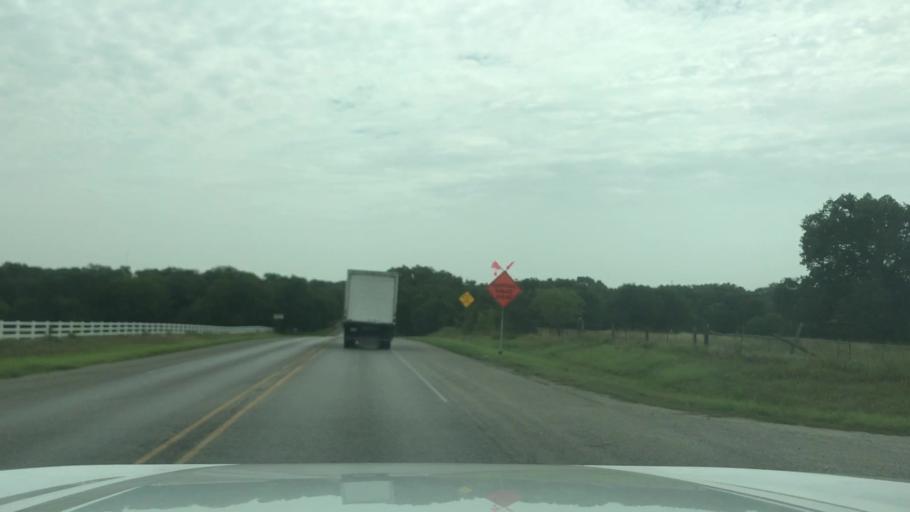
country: US
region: Texas
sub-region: Comanche County
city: De Leon
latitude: 32.1039
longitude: -98.4846
